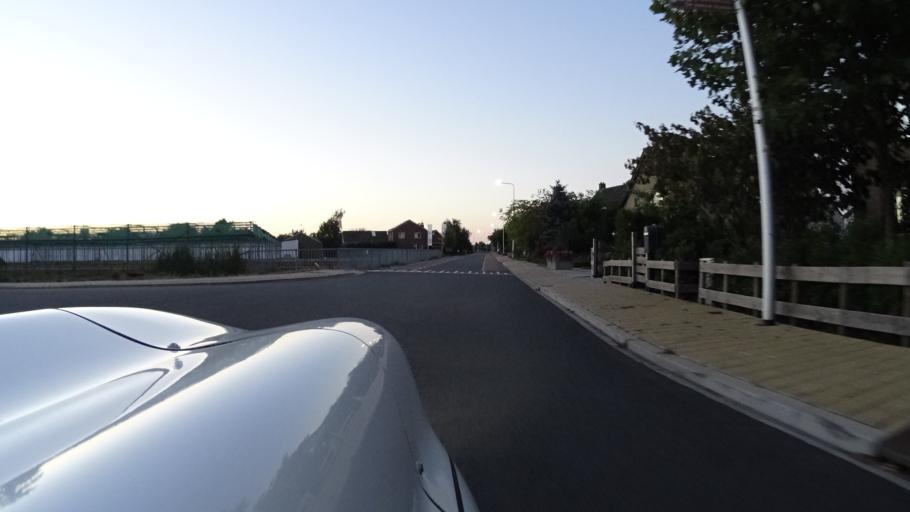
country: NL
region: South Holland
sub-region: Gemeente Kaag en Braassem
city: Oude Wetering
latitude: 52.1930
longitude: 4.6197
